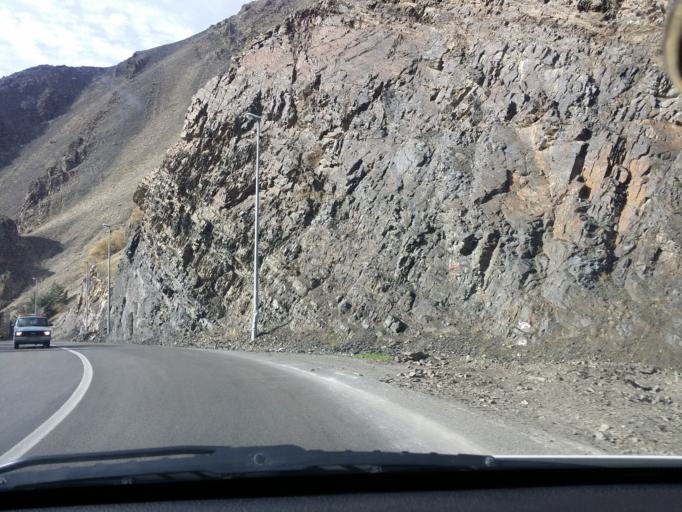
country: IR
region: Alborz
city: Karaj
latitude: 36.0023
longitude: 51.1149
